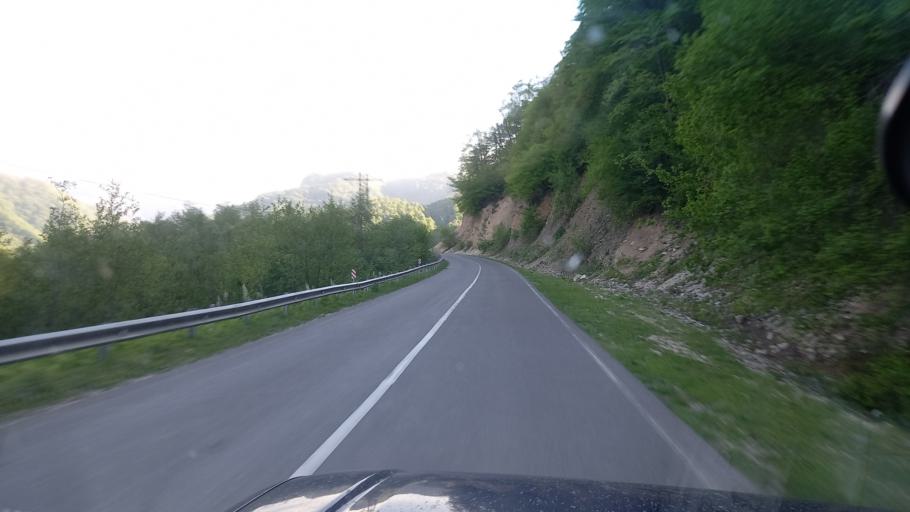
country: RU
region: Ingushetiya
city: Galashki
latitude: 42.9477
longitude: 45.0148
